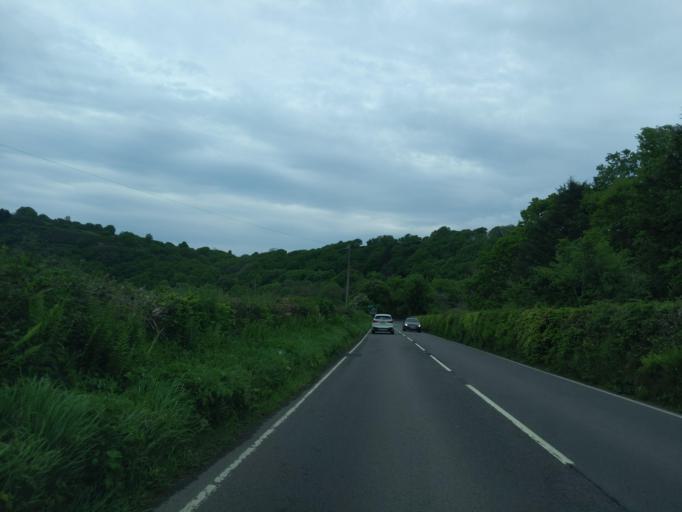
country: GB
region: England
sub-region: Devon
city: Great Torrington
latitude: 50.9437
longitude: -4.1391
